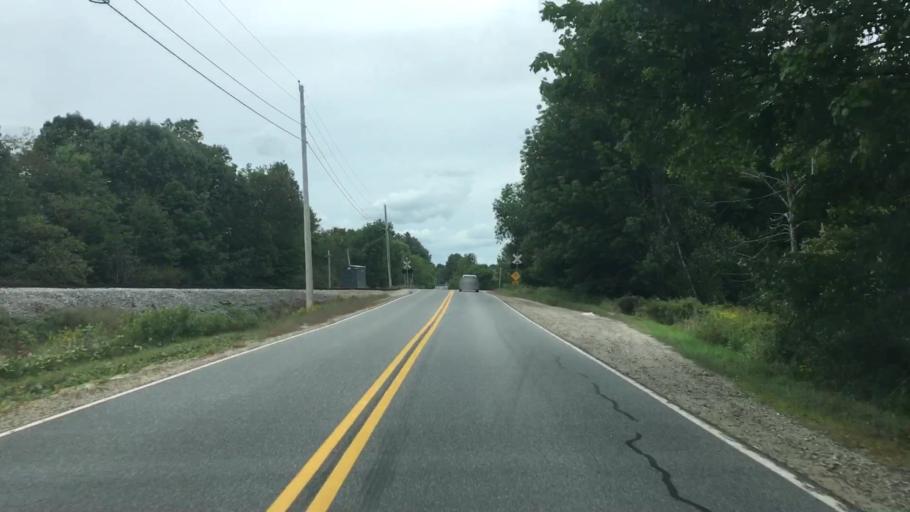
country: US
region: Maine
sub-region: Cumberland County
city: Yarmouth
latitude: 43.8594
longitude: -70.2185
